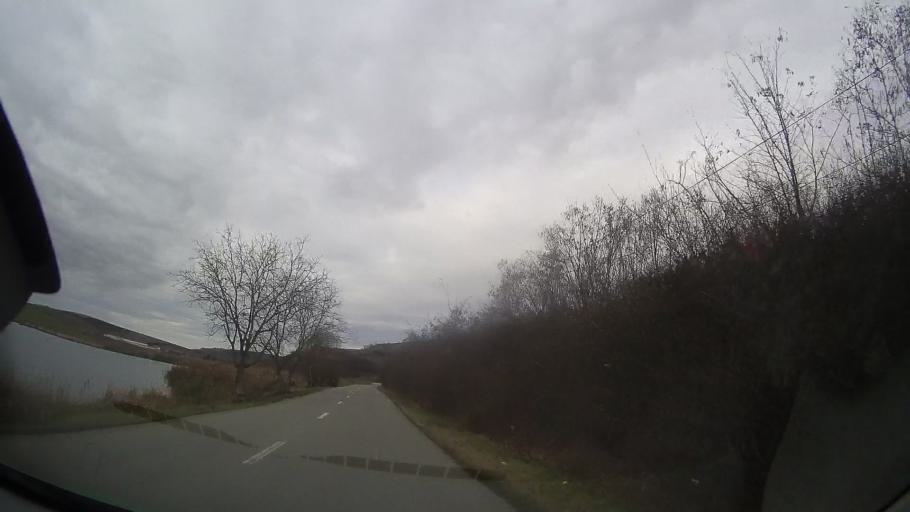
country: RO
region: Mures
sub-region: Comuna Faragau
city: Faragau
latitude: 46.7504
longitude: 24.5269
